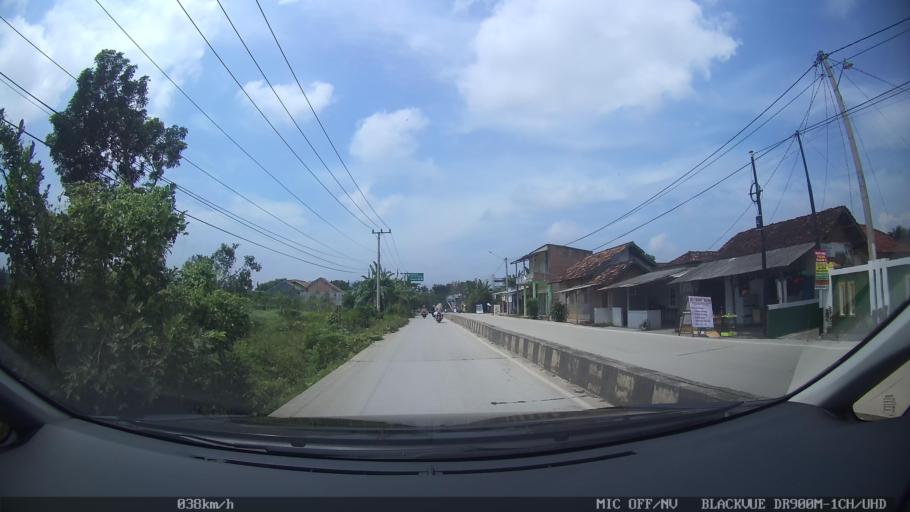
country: ID
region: Lampung
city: Kedaton
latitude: -5.3721
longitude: 105.3085
